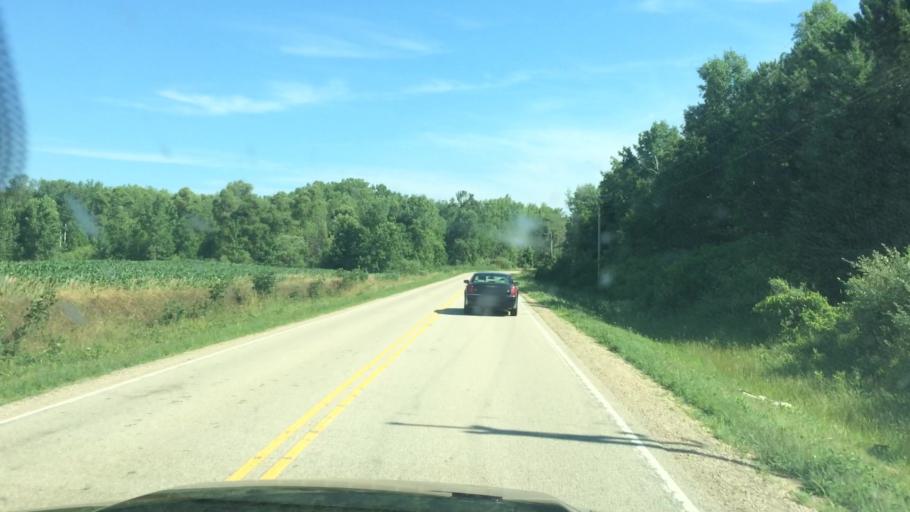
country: US
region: Wisconsin
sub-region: Oconto County
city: Gillett
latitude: 44.7913
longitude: -88.3119
